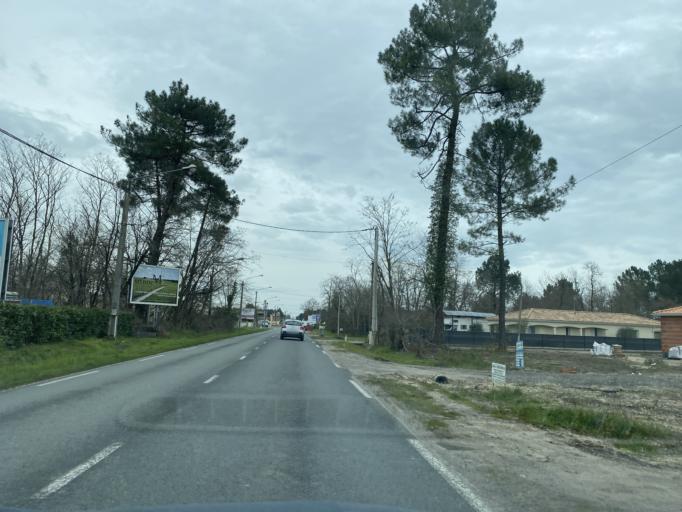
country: FR
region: Aquitaine
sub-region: Departement de la Gironde
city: Parempuyre
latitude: 44.9509
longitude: -0.6301
